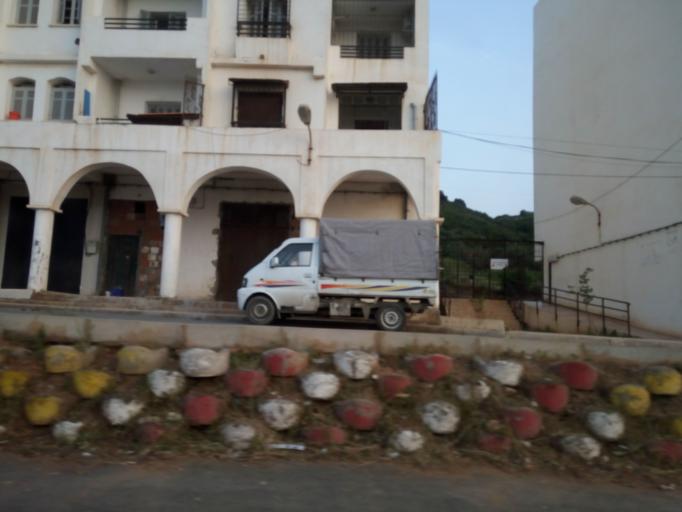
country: DZ
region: Tipaza
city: Bou Ismail
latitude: 36.6073
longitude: 2.6199
